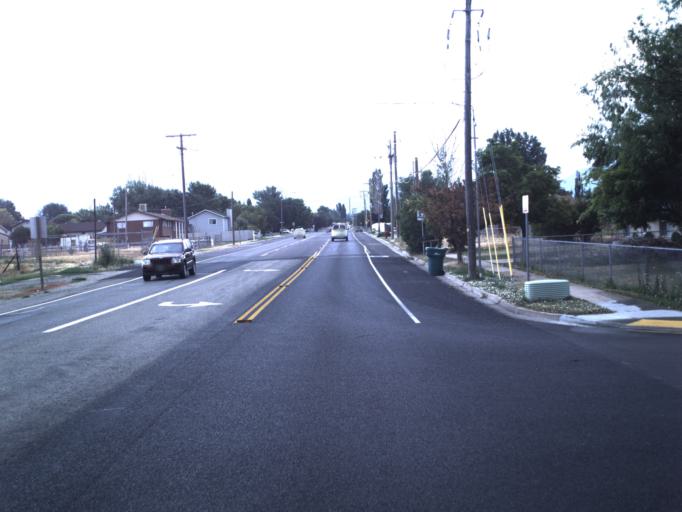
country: US
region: Utah
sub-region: Davis County
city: Clinton
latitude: 41.1637
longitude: -112.0747
